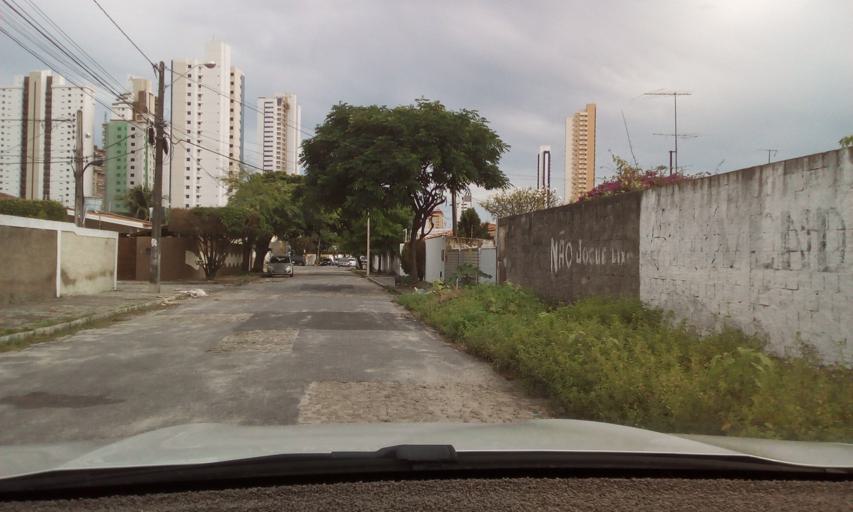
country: BR
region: Paraiba
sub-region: Joao Pessoa
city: Joao Pessoa
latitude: -7.1096
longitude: -34.8538
